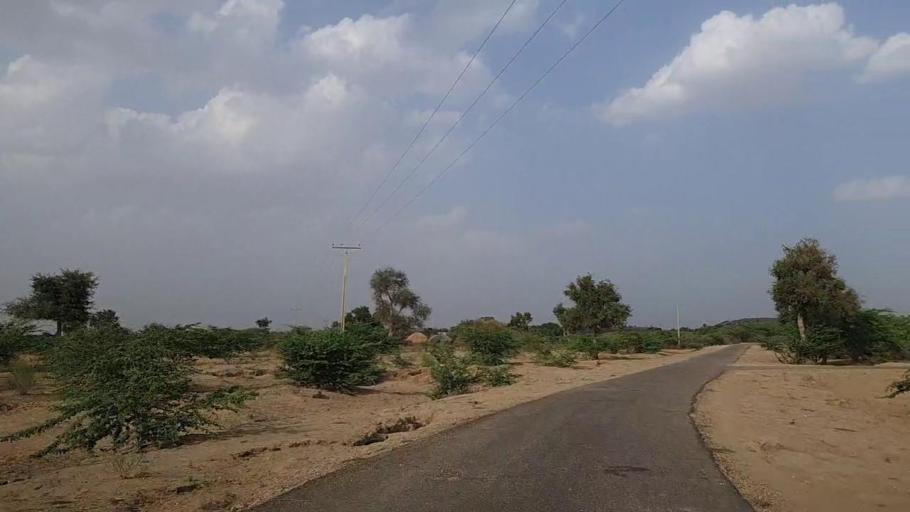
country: PK
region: Sindh
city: Islamkot
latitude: 24.7944
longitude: 70.2025
